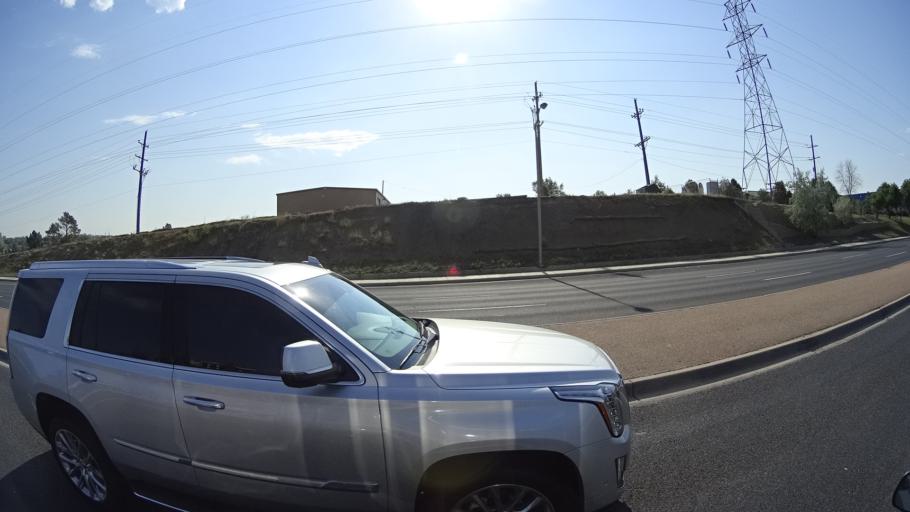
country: US
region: Colorado
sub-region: El Paso County
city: Stratmoor
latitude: 38.8218
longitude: -104.7576
